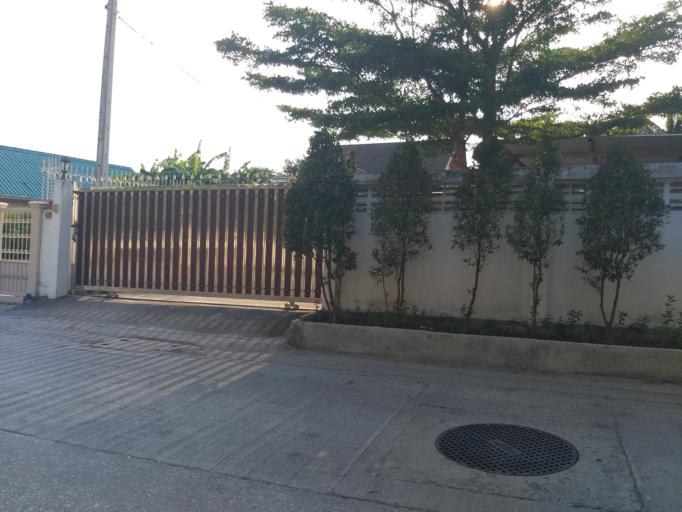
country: TH
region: Bangkok
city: Lat Phrao
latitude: 13.8218
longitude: 100.6121
